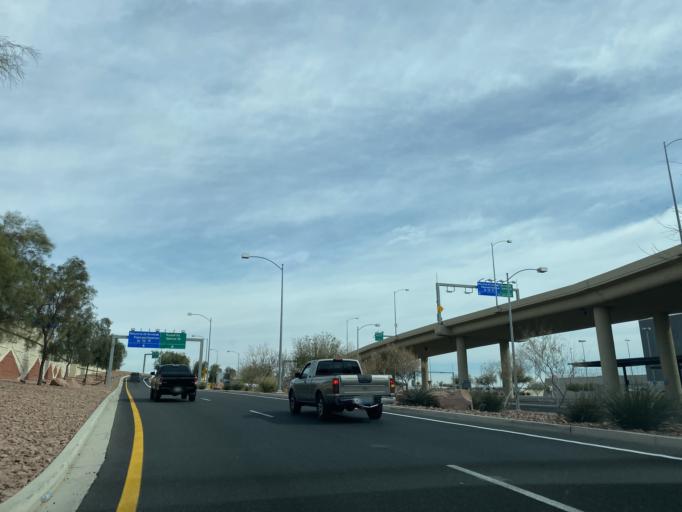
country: US
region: Nevada
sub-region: Clark County
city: Paradise
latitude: 36.0875
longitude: -115.1338
